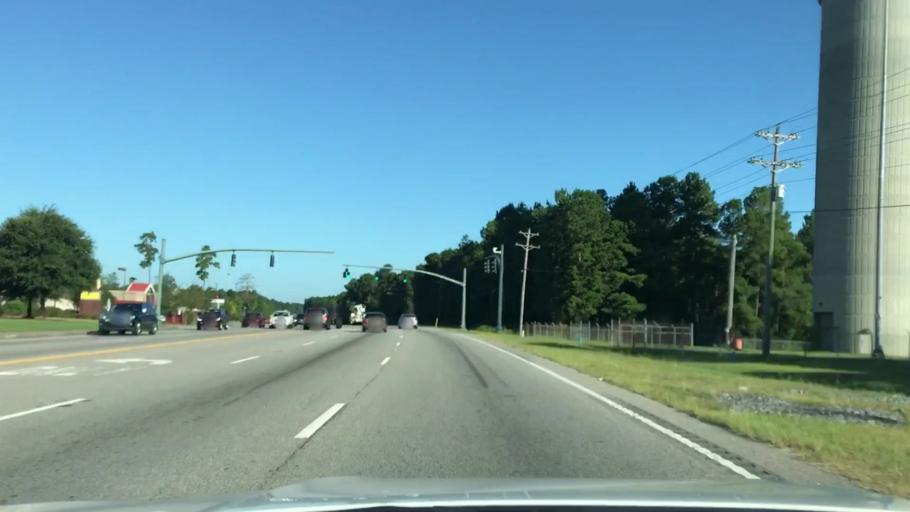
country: US
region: South Carolina
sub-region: Berkeley County
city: Goose Creek
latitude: 33.0354
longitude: -80.0623
